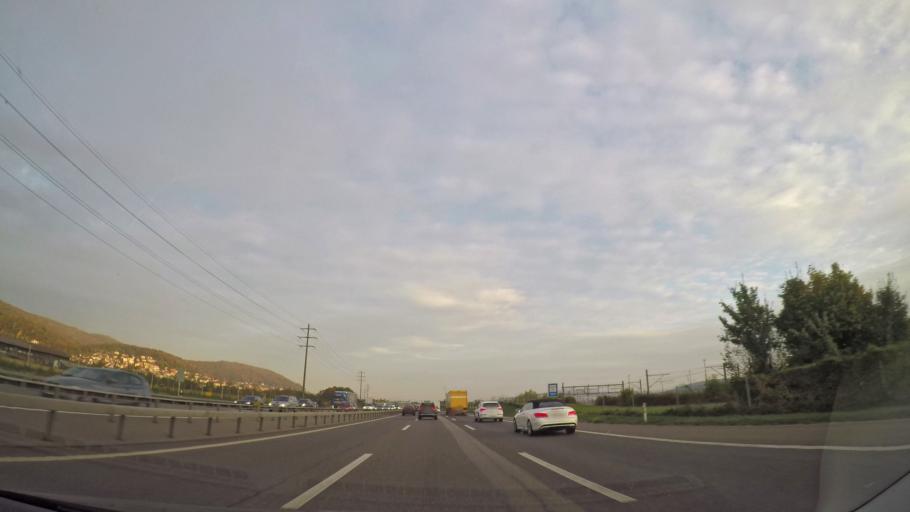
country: CH
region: Aargau
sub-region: Bezirk Baden
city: Spreitenbach
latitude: 47.4246
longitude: 8.3803
